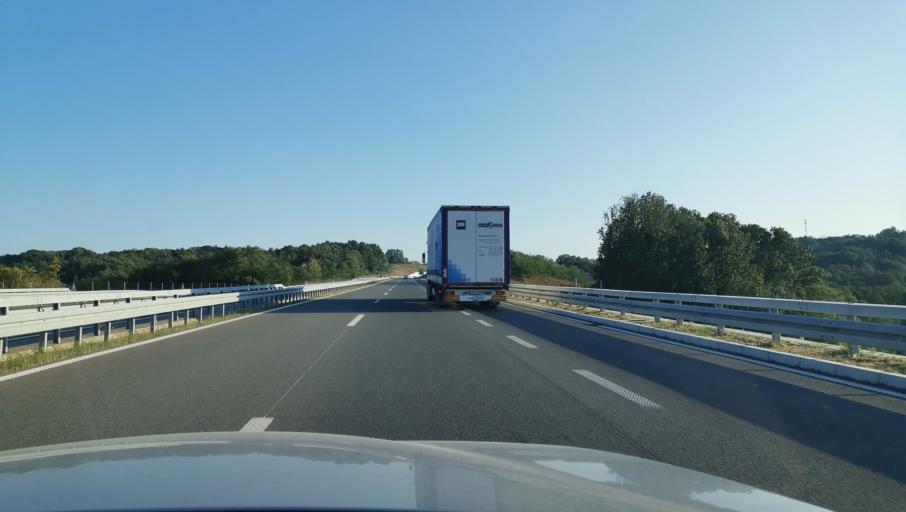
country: RS
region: Central Serbia
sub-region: Moravicki Okrug
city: Gornji Milanovac
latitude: 44.1035
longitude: 20.3846
